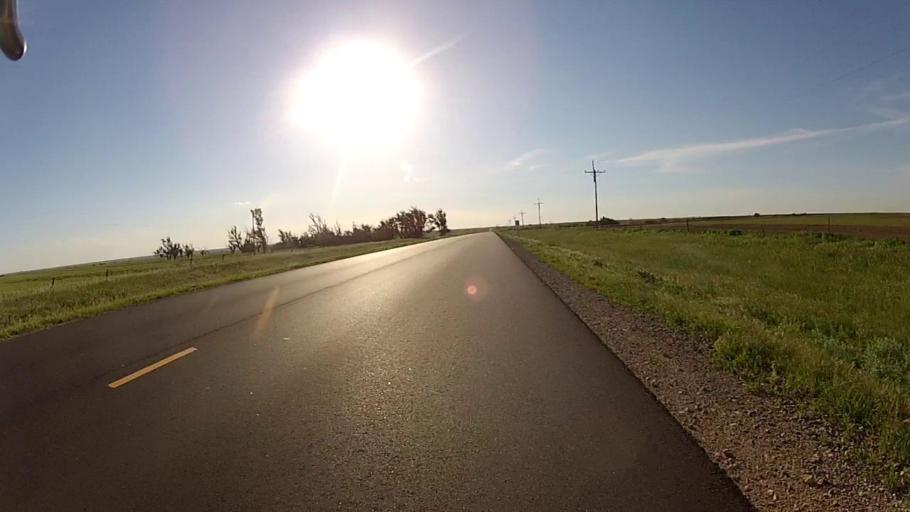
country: US
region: Kansas
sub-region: Comanche County
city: Coldwater
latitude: 37.2820
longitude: -99.1369
